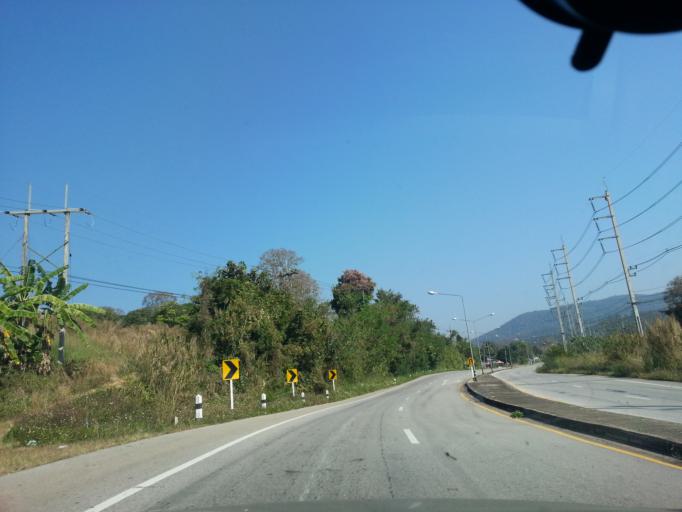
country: TH
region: Chiang Mai
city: Mae Taeng
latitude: 19.2104
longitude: 98.9672
